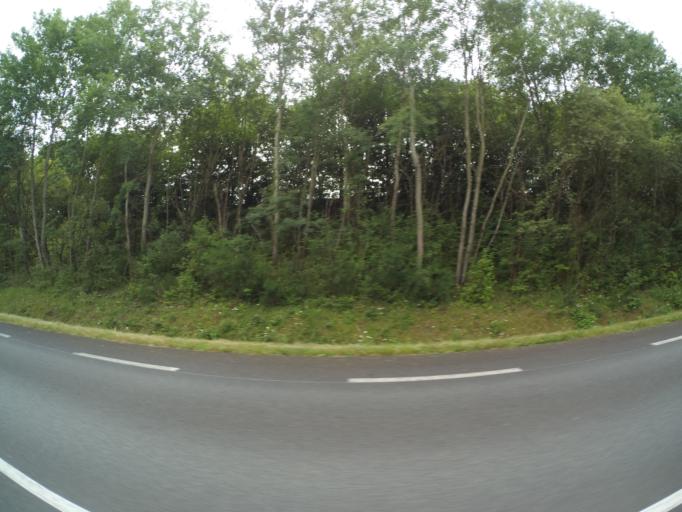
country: FR
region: Pays de la Loire
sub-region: Departement de la Vendee
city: Saint-Georges-de-Montaigu
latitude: 46.9363
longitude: -1.2822
